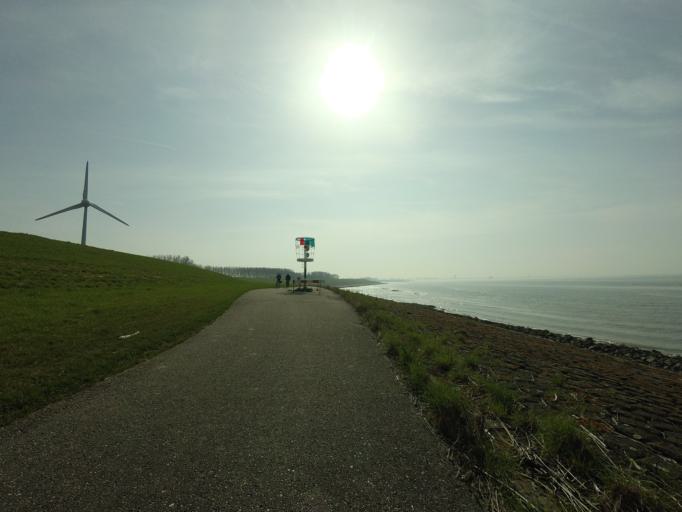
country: NL
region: Zeeland
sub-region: Gemeente Terneuzen
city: Zaamslag
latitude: 51.3568
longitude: 3.9048
